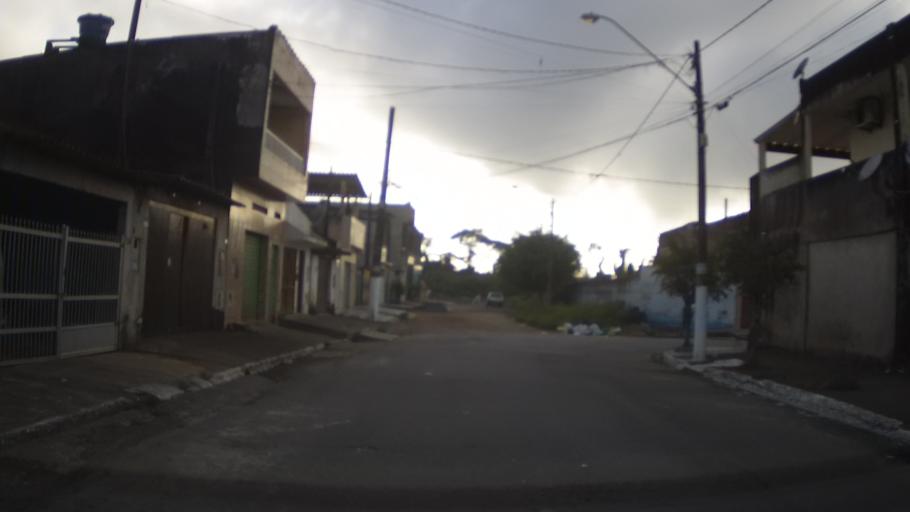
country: BR
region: Sao Paulo
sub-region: Praia Grande
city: Praia Grande
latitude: -24.0128
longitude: -46.4625
